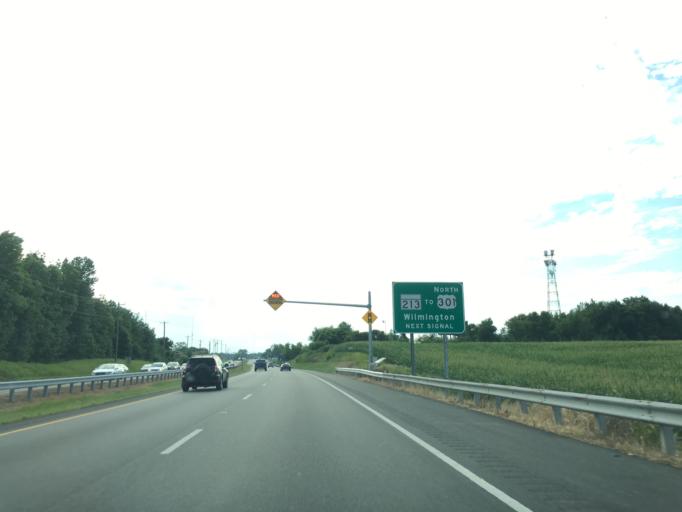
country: US
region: Maryland
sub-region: Queen Anne's County
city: Centreville
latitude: 38.9529
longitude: -76.0722
